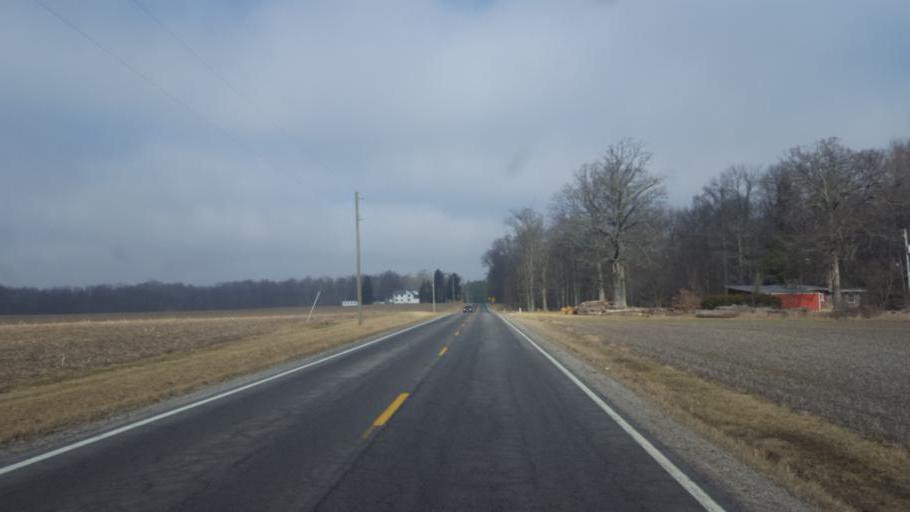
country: US
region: Ohio
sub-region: Crawford County
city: Galion
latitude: 40.7291
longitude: -82.8921
